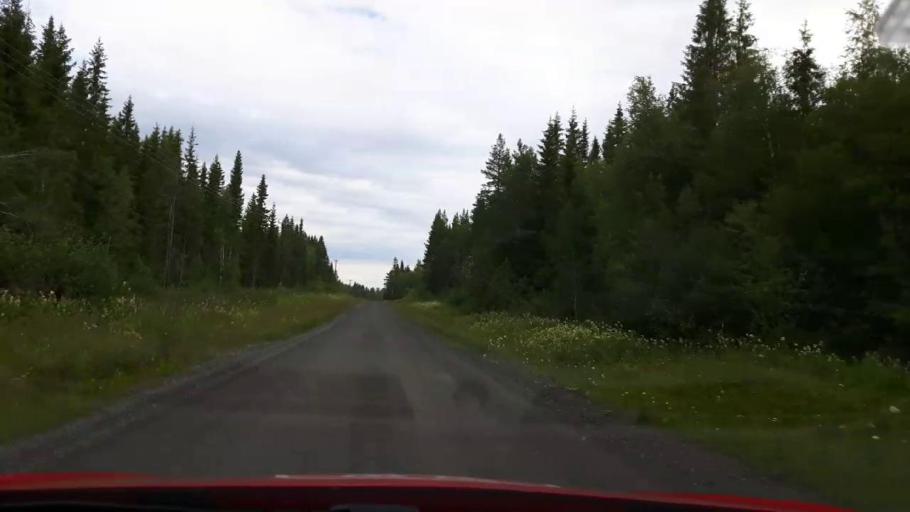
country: SE
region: Jaemtland
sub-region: Stroemsunds Kommun
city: Stroemsund
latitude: 63.5112
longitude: 15.3409
